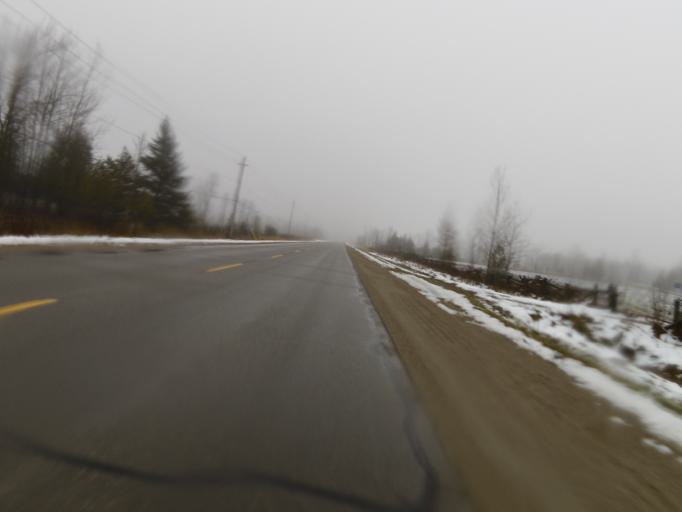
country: CA
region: Ontario
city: Perth
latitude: 44.8308
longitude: -76.3874
